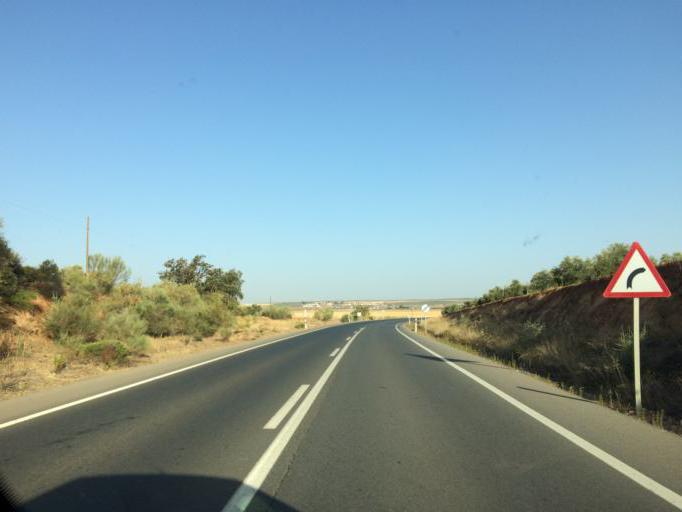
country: ES
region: Andalusia
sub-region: Provincia de Malaga
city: Humilladero
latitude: 37.0592
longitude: -4.6894
